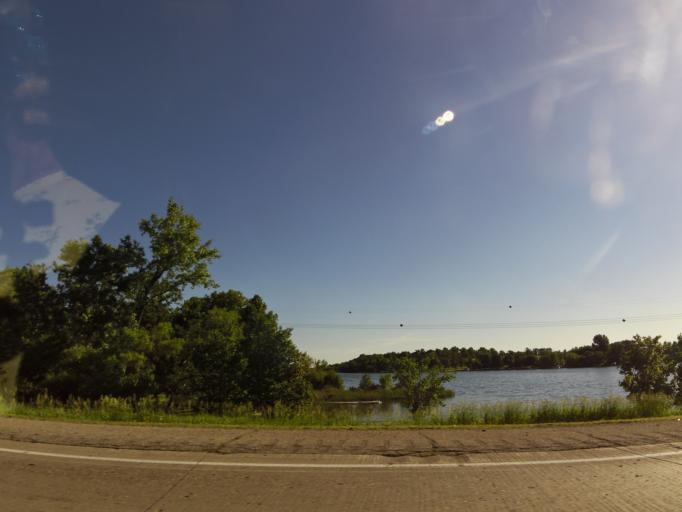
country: US
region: Minnesota
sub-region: Douglas County
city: Alexandria
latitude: 45.8650
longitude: -95.4360
